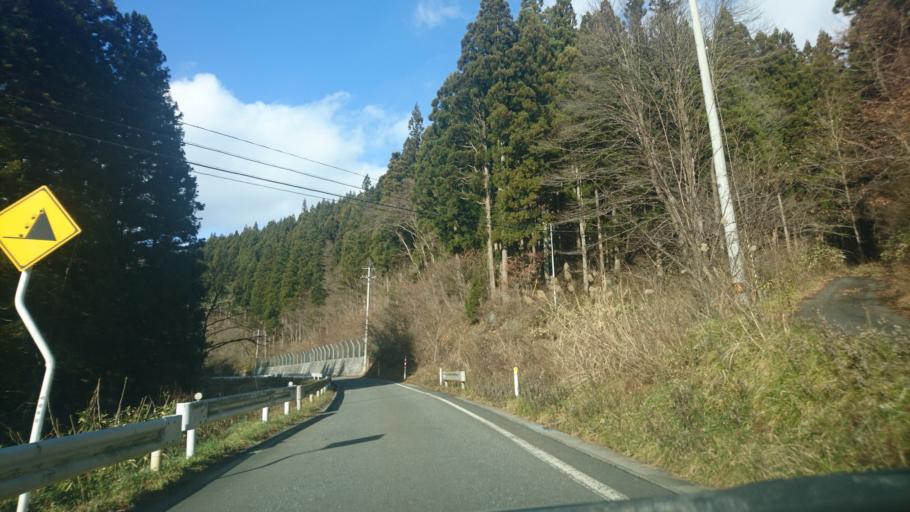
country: JP
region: Iwate
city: Mizusawa
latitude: 39.0955
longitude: 141.3861
